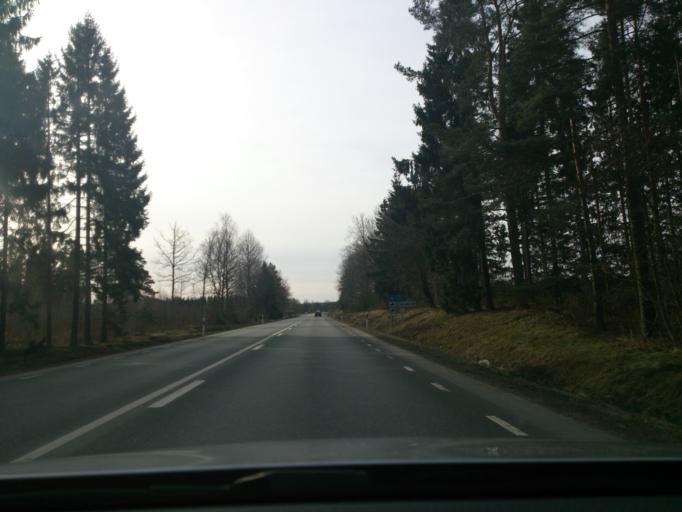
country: SE
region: Kronoberg
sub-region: Alvesta Kommun
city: Moheda
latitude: 56.9683
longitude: 14.5708
